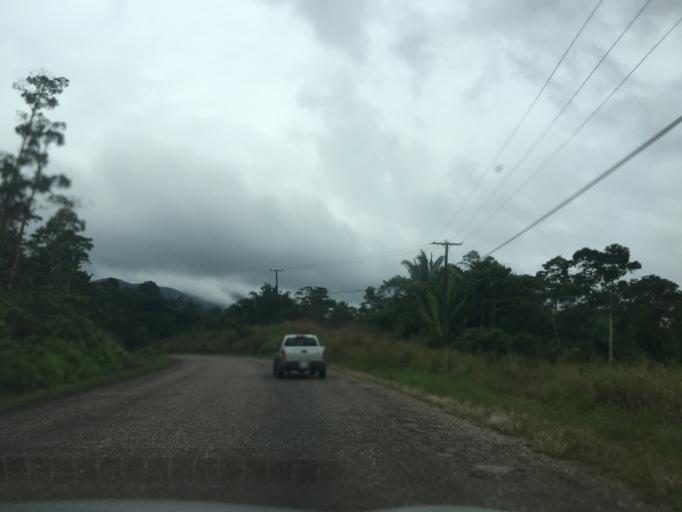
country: BZ
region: Cayo
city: Belmopan
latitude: 17.0502
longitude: -88.5573
